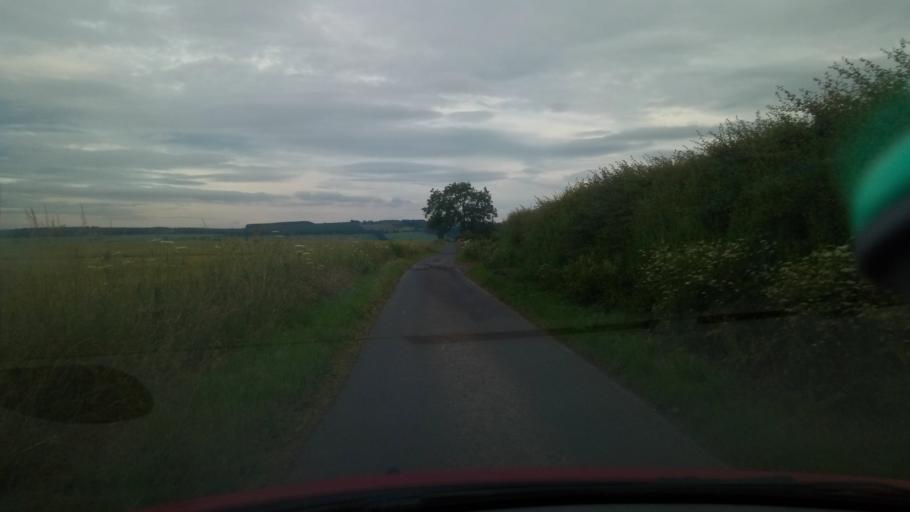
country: GB
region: Scotland
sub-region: The Scottish Borders
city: Saint Boswells
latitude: 55.5052
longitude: -2.6269
